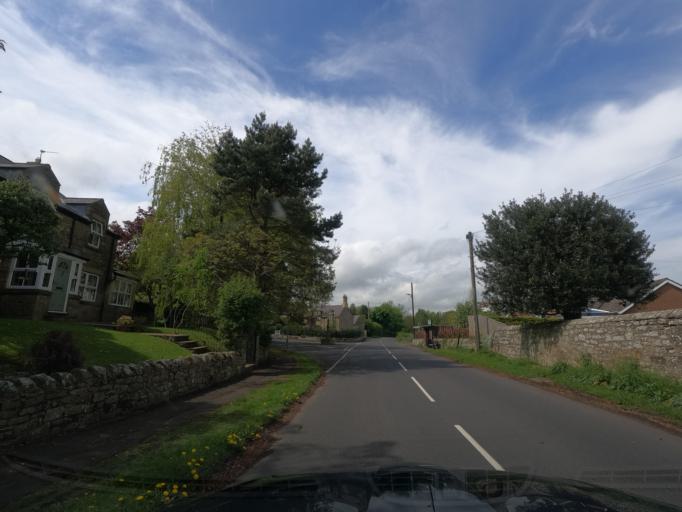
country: GB
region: England
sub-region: Northumberland
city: Whittingham
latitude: 55.4007
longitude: -1.8894
